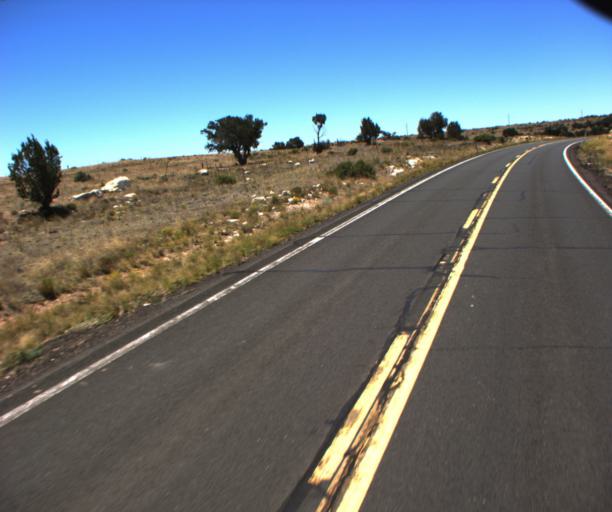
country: US
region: Arizona
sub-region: Coconino County
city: LeChee
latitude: 34.7702
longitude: -111.0077
